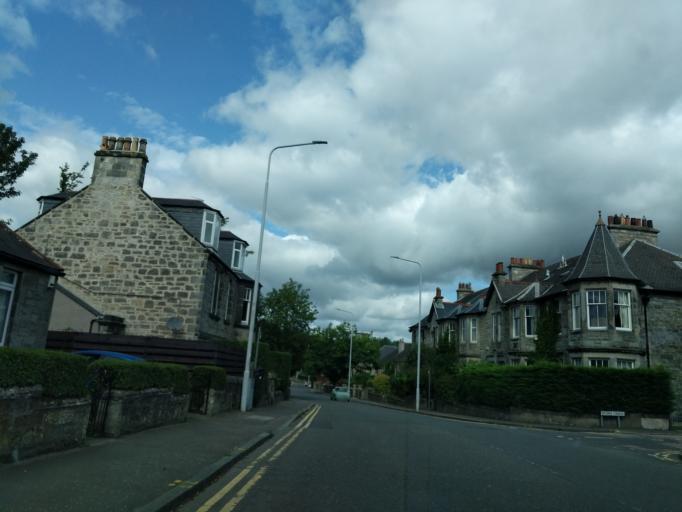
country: GB
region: Scotland
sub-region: Fife
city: Dunfermline
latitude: 56.0768
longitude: -3.4614
